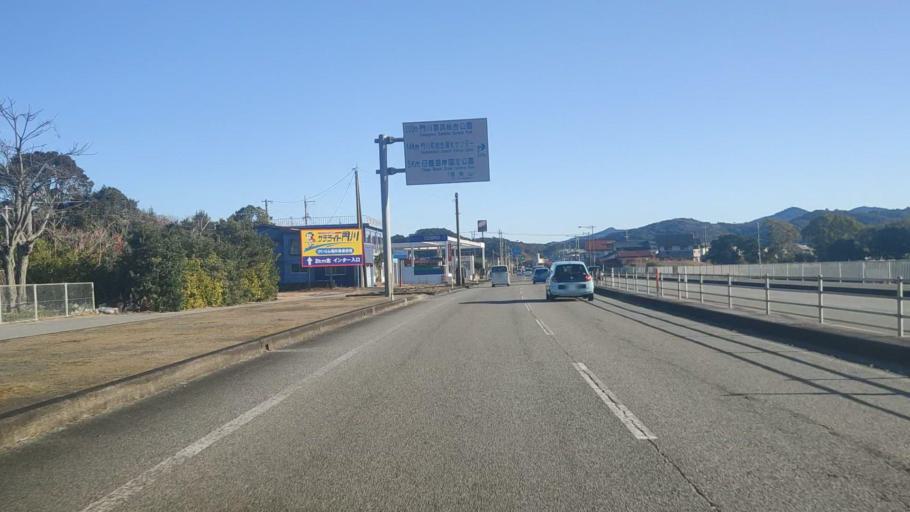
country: JP
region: Miyazaki
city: Nobeoka
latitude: 32.4833
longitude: 131.6592
